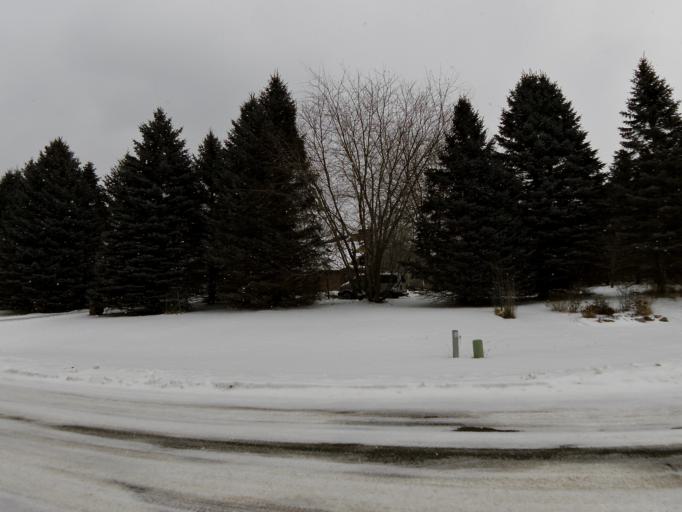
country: US
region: Minnesota
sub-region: Washington County
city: Lake Elmo
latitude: 44.9712
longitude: -92.8421
